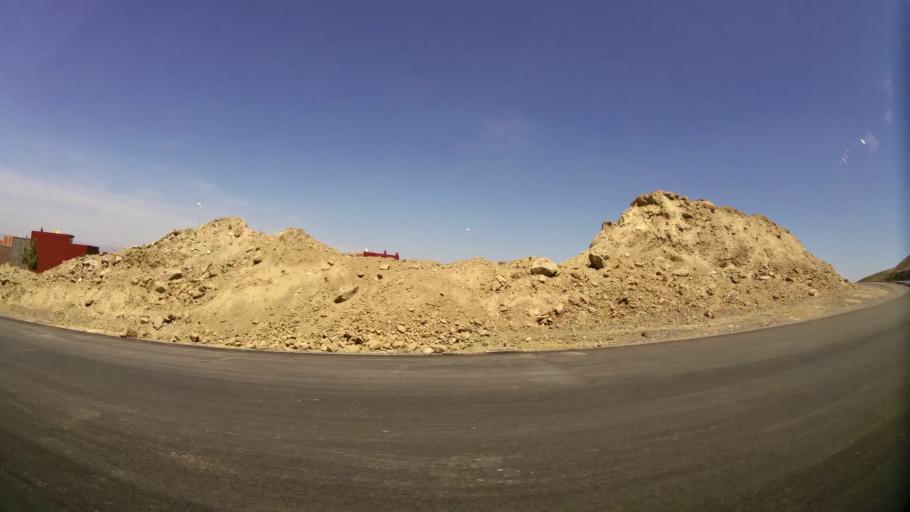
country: MA
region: Oriental
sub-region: Oujda-Angad
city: Oujda
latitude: 34.6513
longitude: -1.9222
